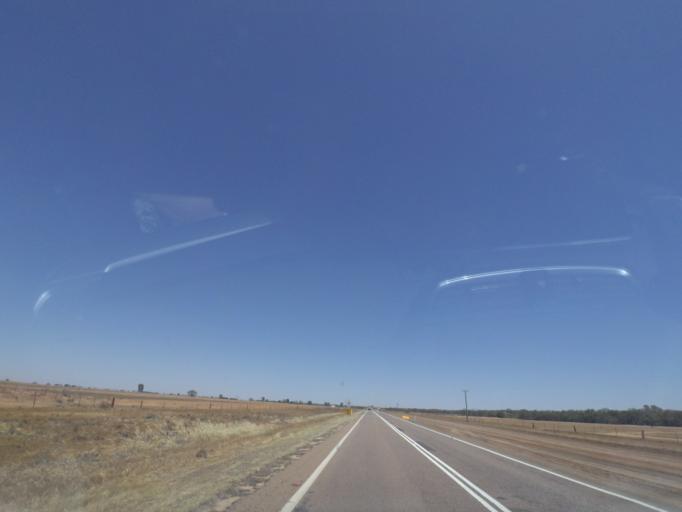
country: AU
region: New South Wales
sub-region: Berrigan
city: Berrigan
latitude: -35.1495
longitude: 145.9955
